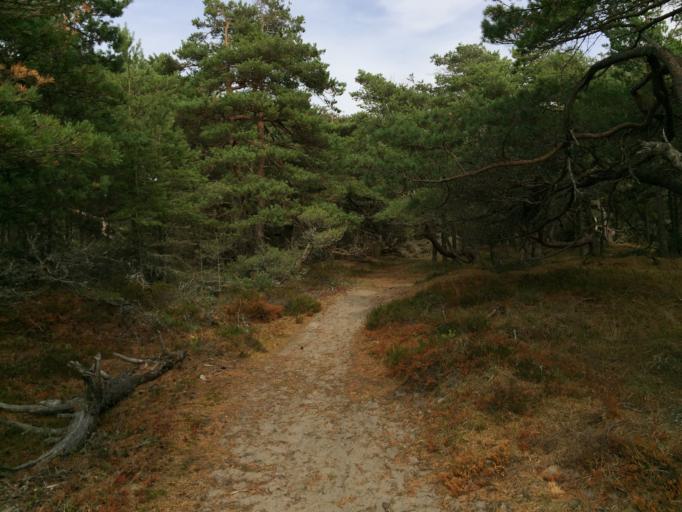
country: NO
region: Ostfold
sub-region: Hvaler
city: Skjaerhalden
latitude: 59.0258
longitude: 11.0192
